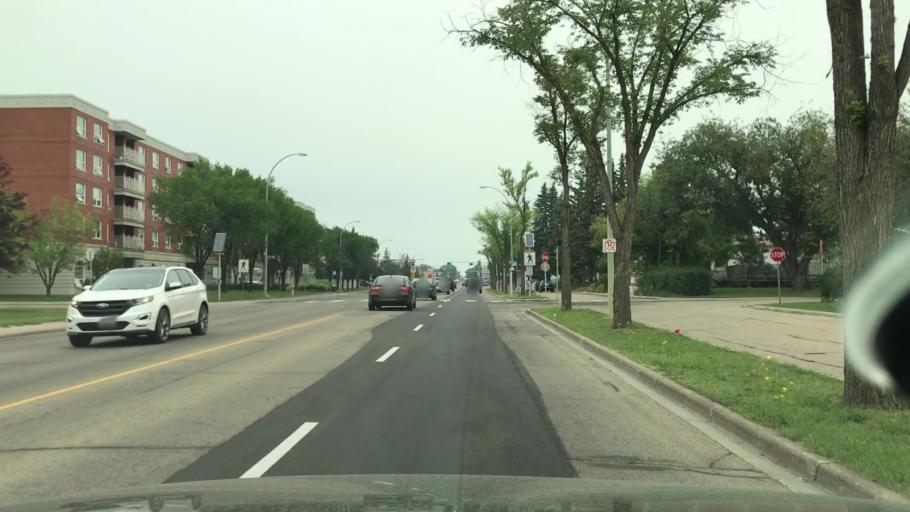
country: CA
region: Alberta
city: Edmonton
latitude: 53.5373
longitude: -113.5779
